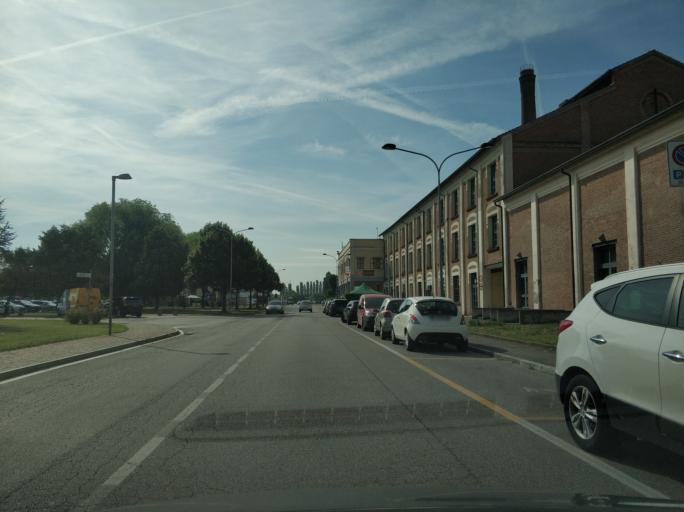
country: IT
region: Veneto
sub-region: Provincia di Padova
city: Este
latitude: 45.2184
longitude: 11.6731
